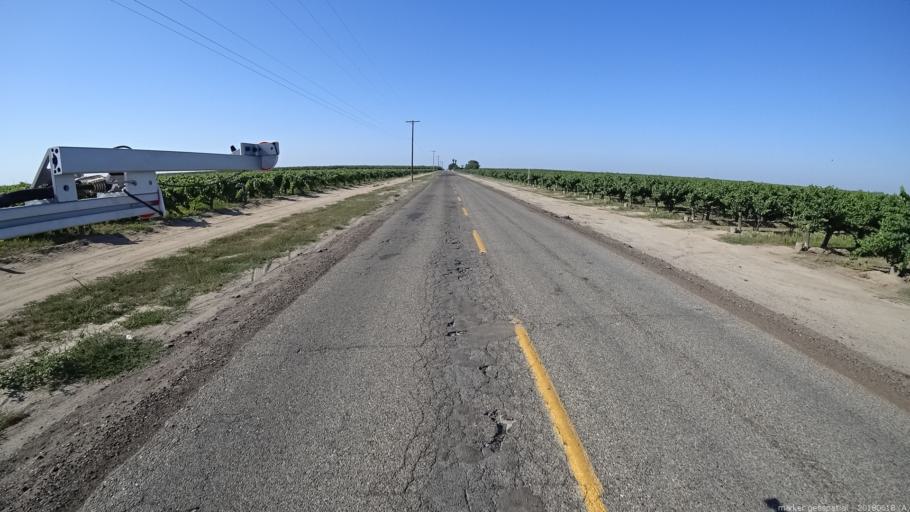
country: US
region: California
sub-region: Madera County
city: Madera
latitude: 36.9214
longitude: -120.1288
